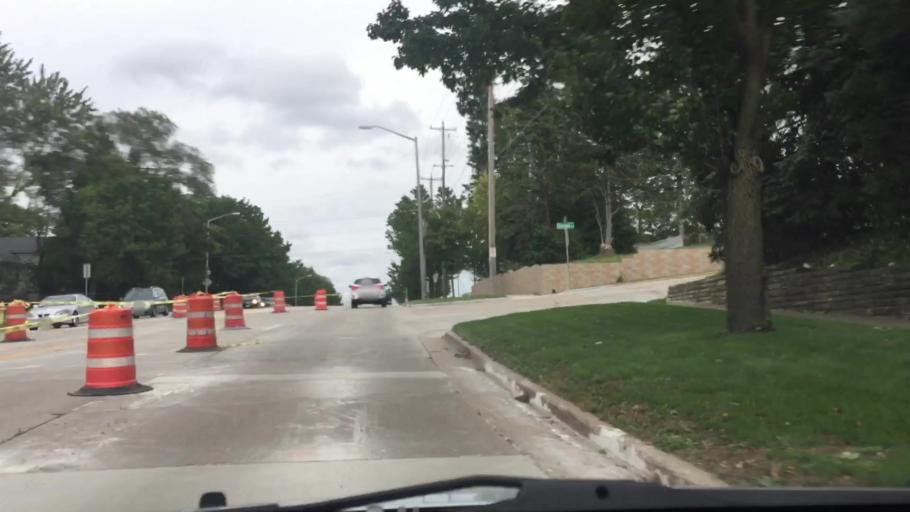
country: US
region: Wisconsin
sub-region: Waukesha County
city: Waukesha
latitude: 42.9882
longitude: -88.2311
